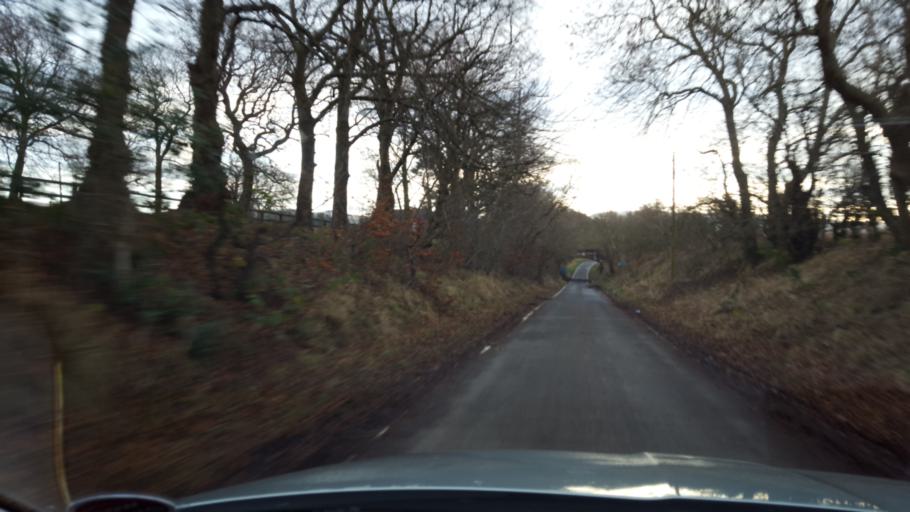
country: GB
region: Scotland
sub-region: West Lothian
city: Mid Calder
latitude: 55.8528
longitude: -3.5096
